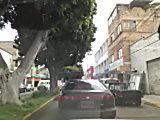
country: MX
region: Nayarit
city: Tepic
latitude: 21.5064
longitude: -104.8916
